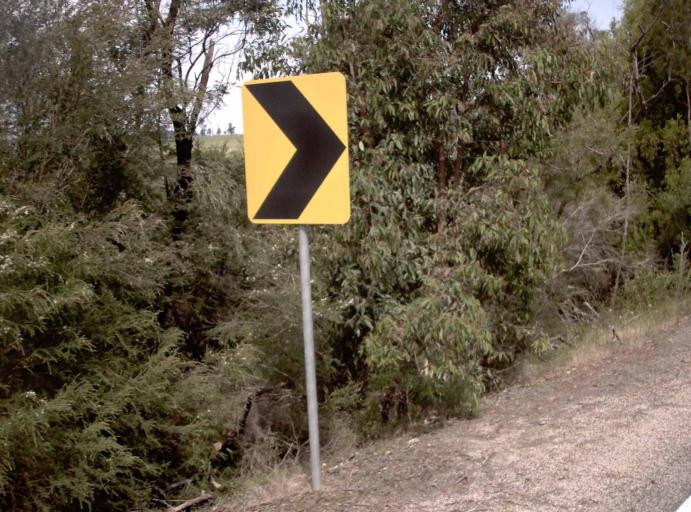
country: AU
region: New South Wales
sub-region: Bega Valley
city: Eden
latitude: -37.4809
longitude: 149.6413
